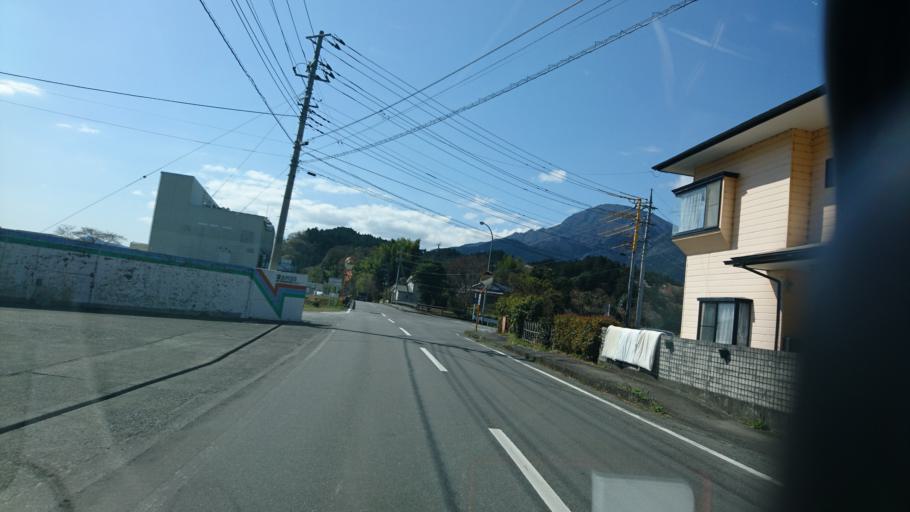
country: JP
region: Shizuoka
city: Fujinomiya
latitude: 35.2987
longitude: 138.4509
